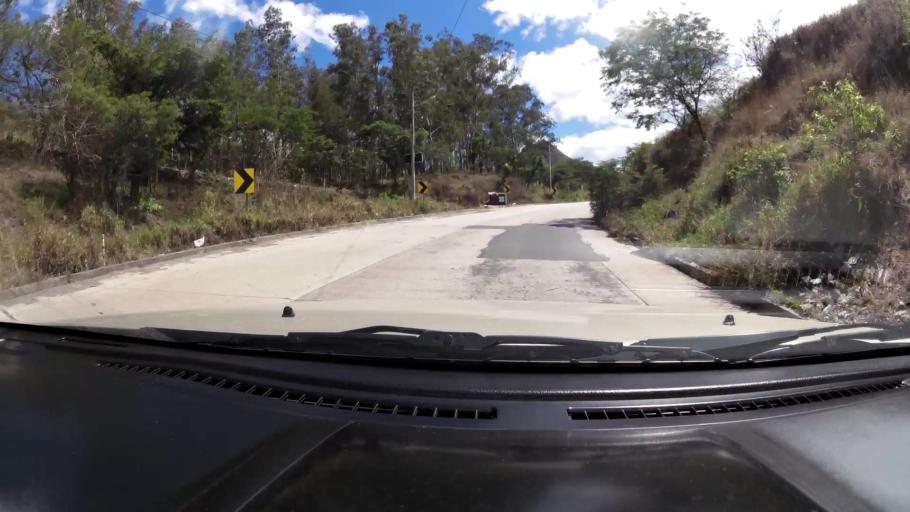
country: EC
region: Azuay
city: Cuenca
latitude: -3.2191
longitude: -79.2029
